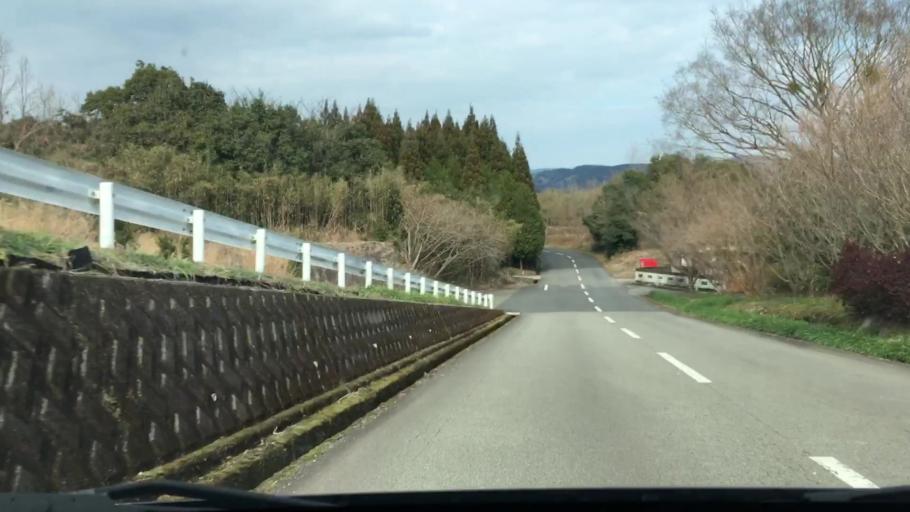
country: JP
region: Miyazaki
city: Nichinan
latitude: 31.6184
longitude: 131.3356
